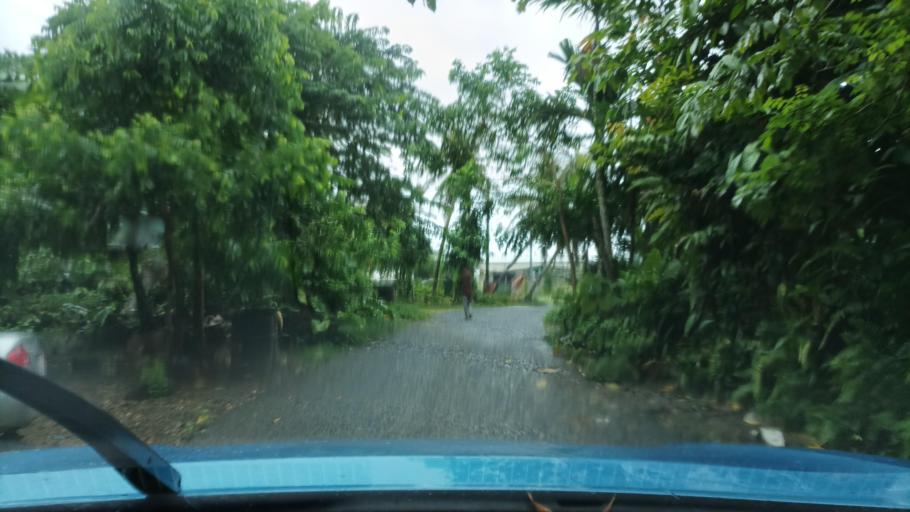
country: FM
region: Pohnpei
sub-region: Kolonia Municipality
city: Kolonia
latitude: 6.9584
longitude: 158.2125
